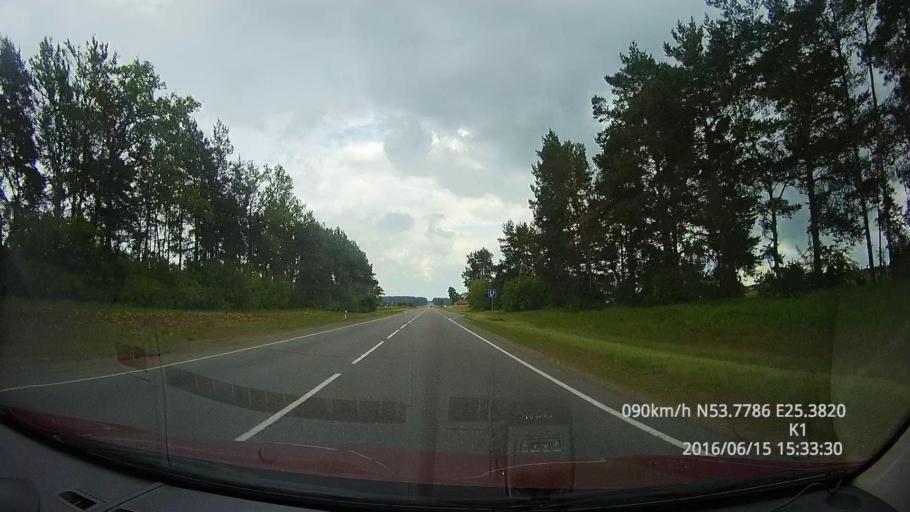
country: BY
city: Berezovka
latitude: 53.7779
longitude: 25.3823
